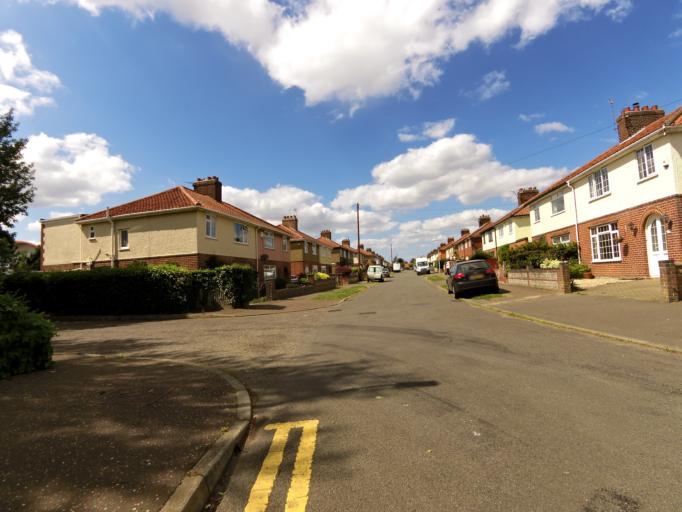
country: GB
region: England
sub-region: Norfolk
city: Norwich
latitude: 52.6556
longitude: 1.2727
